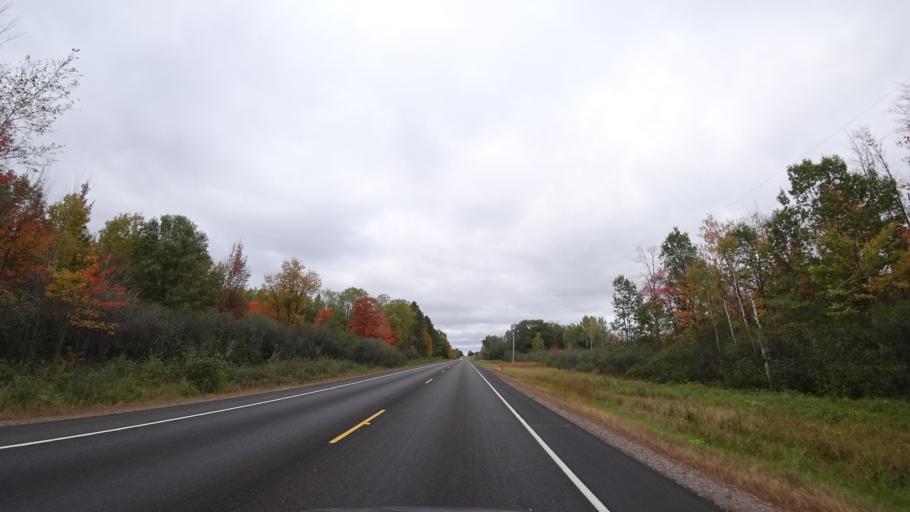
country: US
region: Wisconsin
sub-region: Rusk County
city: Ladysmith
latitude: 45.3522
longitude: -91.1108
